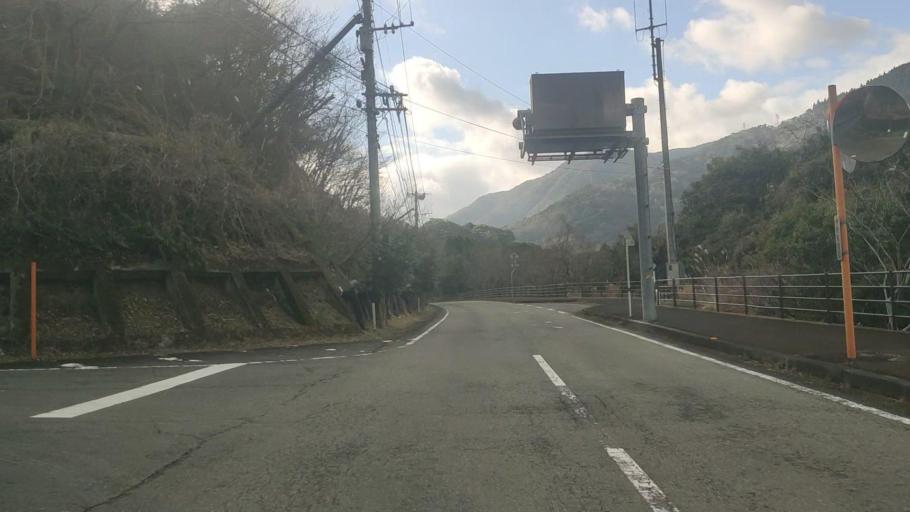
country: JP
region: Kumamoto
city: Hitoyoshi
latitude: 32.3850
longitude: 130.8351
